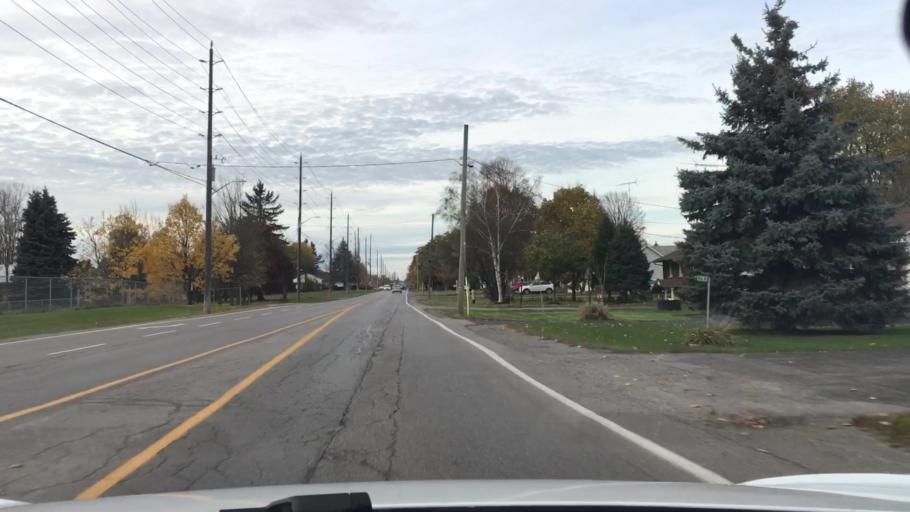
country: CA
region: Ontario
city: Oshawa
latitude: 43.9407
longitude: -78.8283
